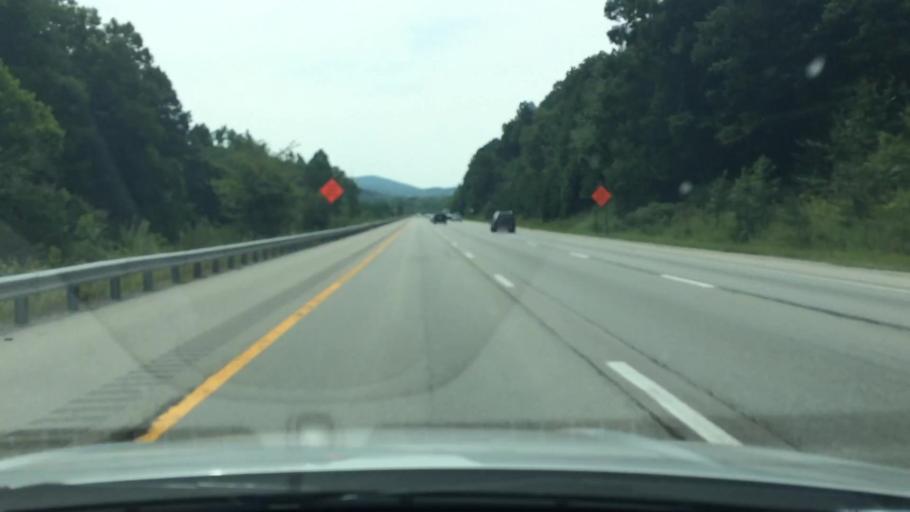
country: US
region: Kentucky
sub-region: Madison County
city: Berea
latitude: 37.5290
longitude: -84.3207
